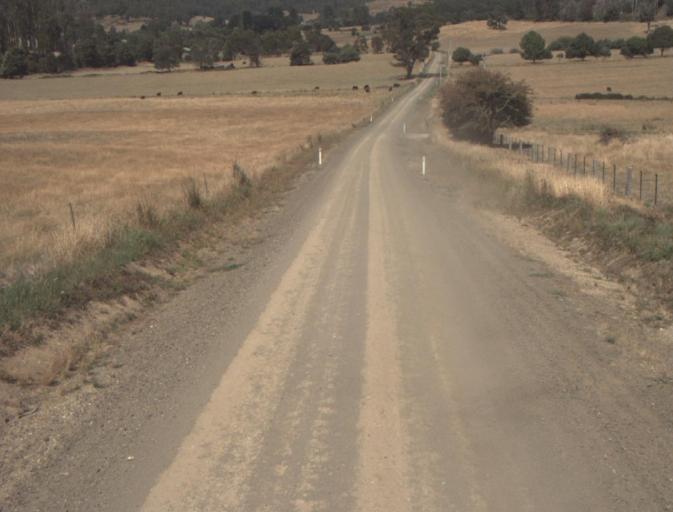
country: AU
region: Tasmania
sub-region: Launceston
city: Mayfield
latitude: -41.2512
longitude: 147.1340
